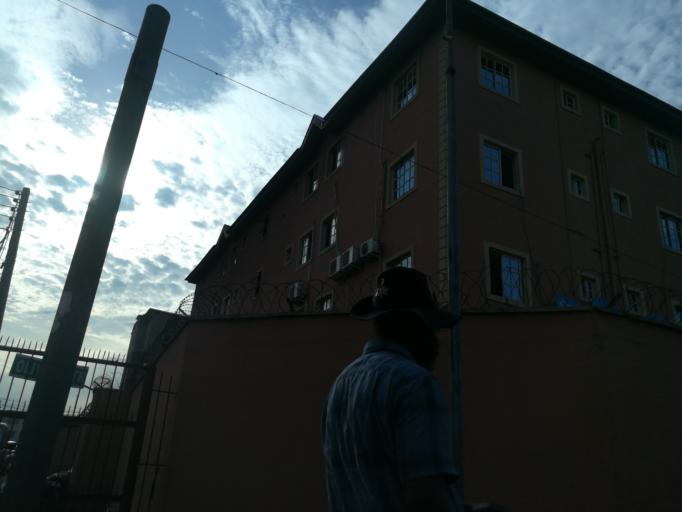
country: NG
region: Lagos
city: Ikeja
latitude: 6.5951
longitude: 3.3460
